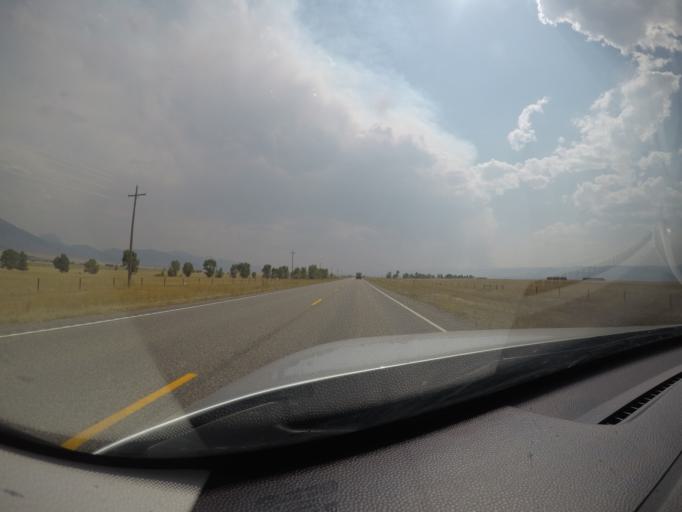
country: US
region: Montana
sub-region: Madison County
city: Virginia City
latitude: 45.2503
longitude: -111.6789
